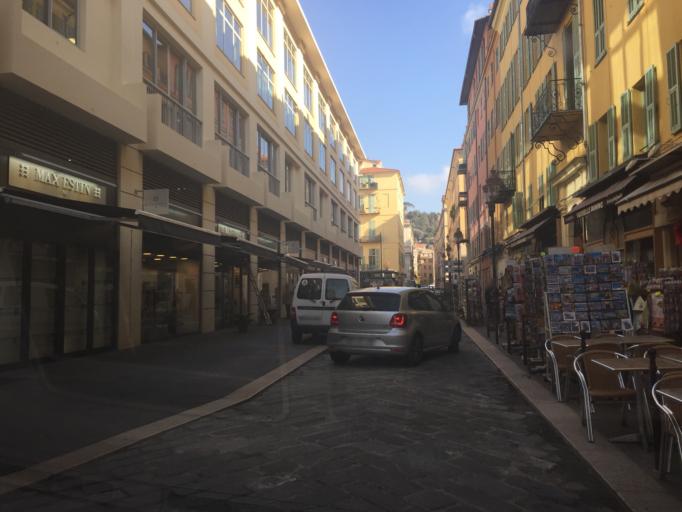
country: FR
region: Provence-Alpes-Cote d'Azur
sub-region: Departement des Alpes-Maritimes
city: Nice
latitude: 43.6965
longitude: 7.2720
